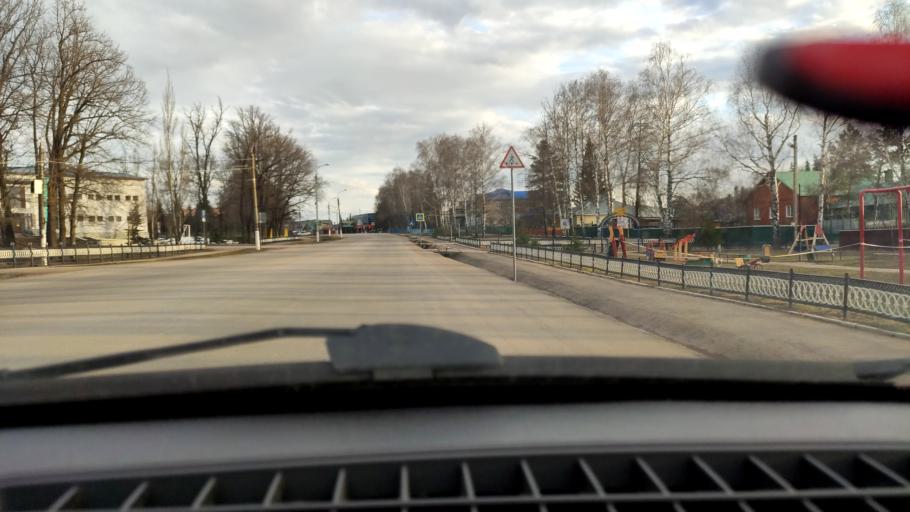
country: RU
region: Bashkortostan
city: Tolbazy
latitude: 54.0135
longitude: 55.8863
